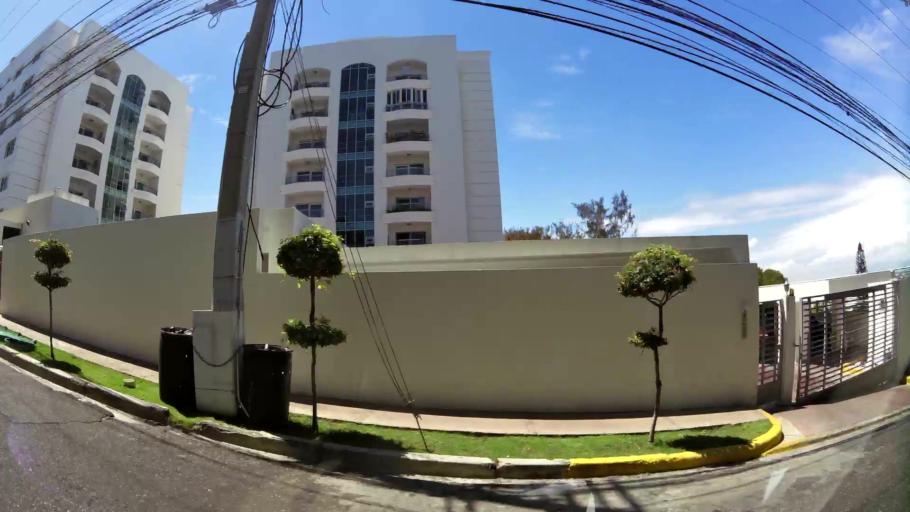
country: DO
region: Santiago
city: Santiago de los Caballeros
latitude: 19.4565
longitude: -70.6917
